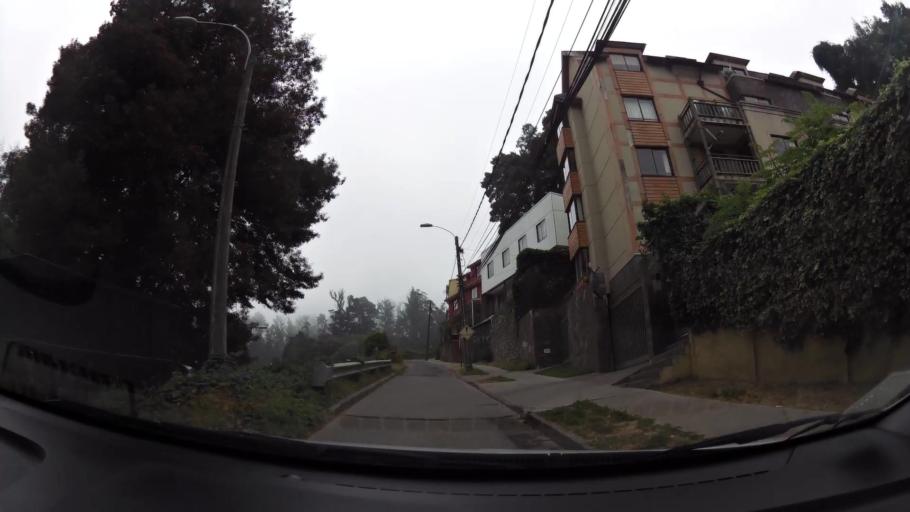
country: CL
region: Biobio
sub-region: Provincia de Concepcion
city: Concepcion
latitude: -36.8333
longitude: -73.0369
